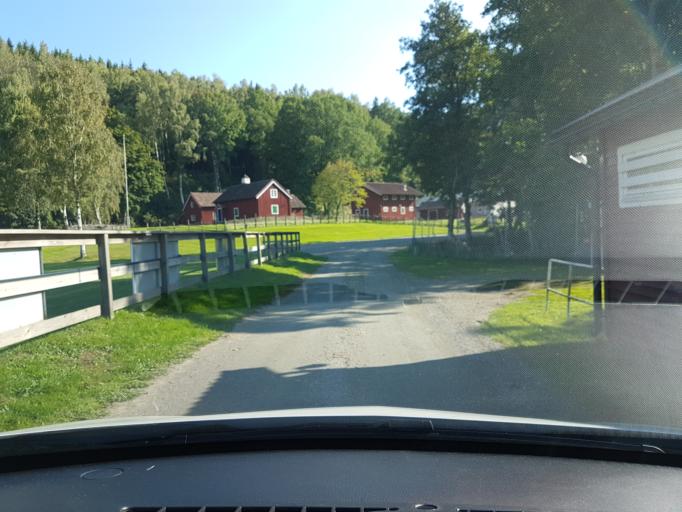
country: SE
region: Vaestra Goetaland
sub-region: Ale Kommun
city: Skepplanda
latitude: 57.9769
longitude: 12.1936
